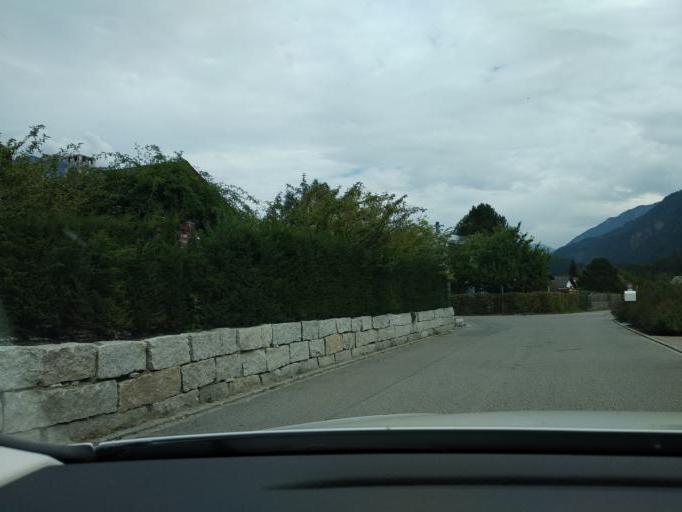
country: CH
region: Grisons
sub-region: Imboden District
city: Bonaduz
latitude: 46.8099
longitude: 9.4038
